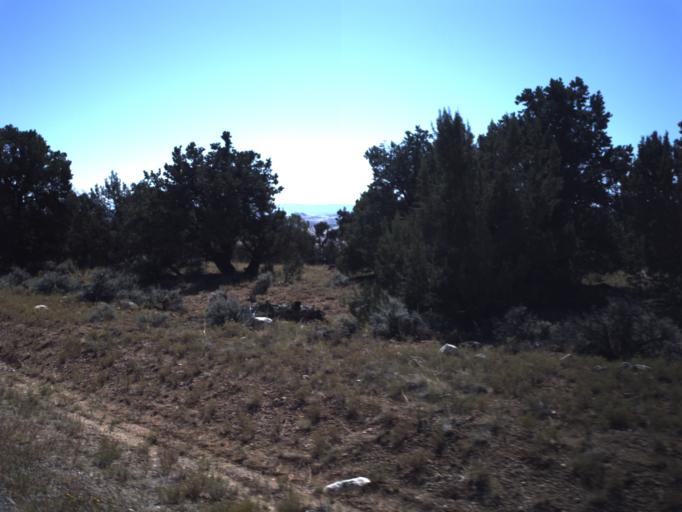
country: US
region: Utah
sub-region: Wayne County
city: Loa
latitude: 37.8775
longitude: -111.4537
